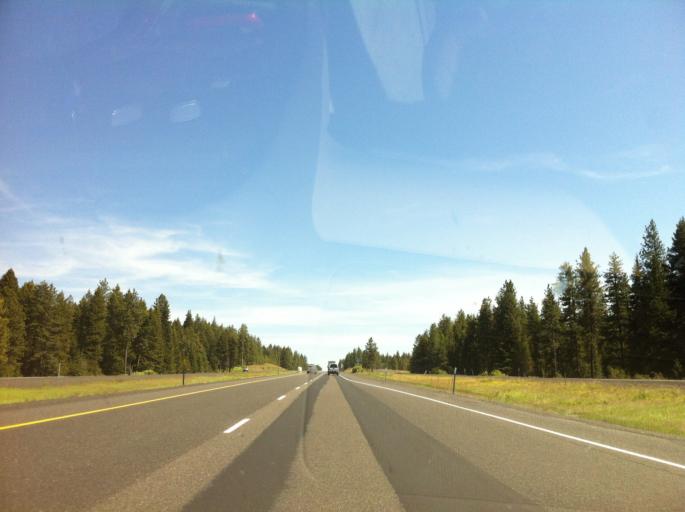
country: US
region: Oregon
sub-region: Umatilla County
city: Mission
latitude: 45.5037
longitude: -118.4238
